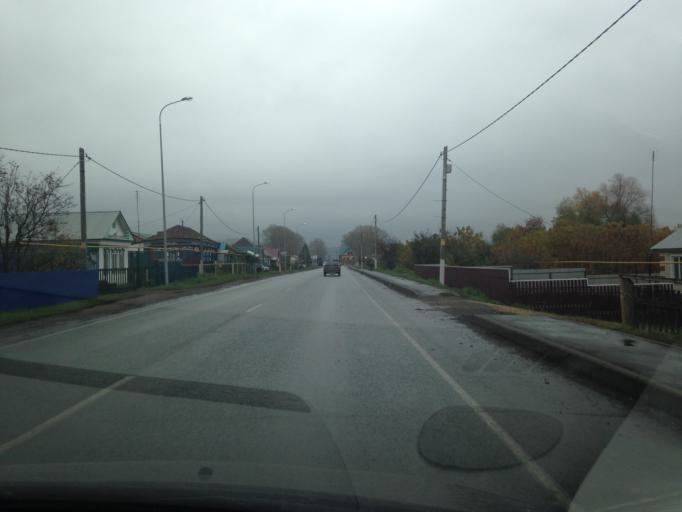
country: RU
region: Tatarstan
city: Buinsk
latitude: 54.9957
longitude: 48.3343
